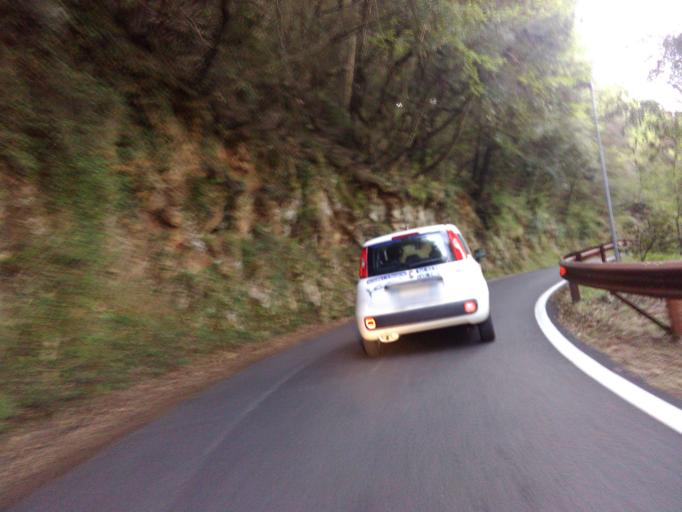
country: IT
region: Tuscany
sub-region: Provincia di Lucca
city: Pontestazzemese
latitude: 43.9606
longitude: 10.2778
